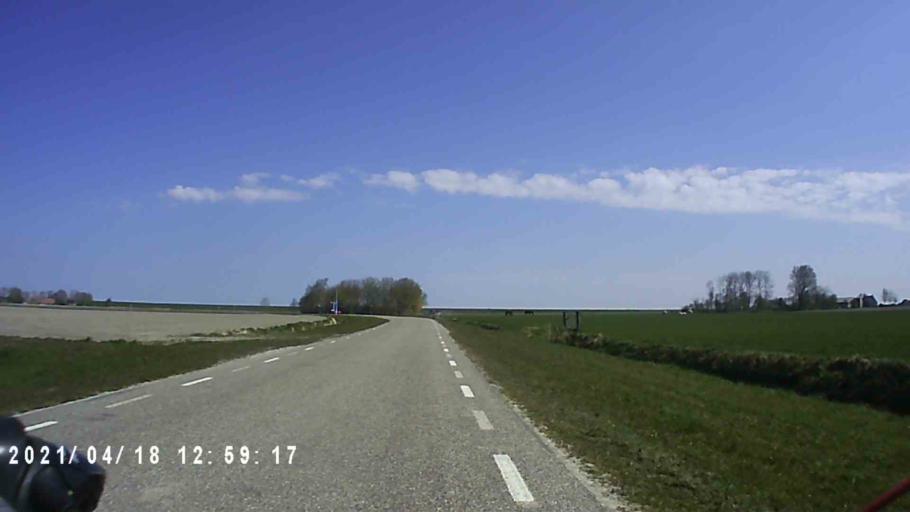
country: NL
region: Friesland
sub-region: Gemeente Dongeradeel
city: Anjum
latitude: 53.3955
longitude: 6.0891
